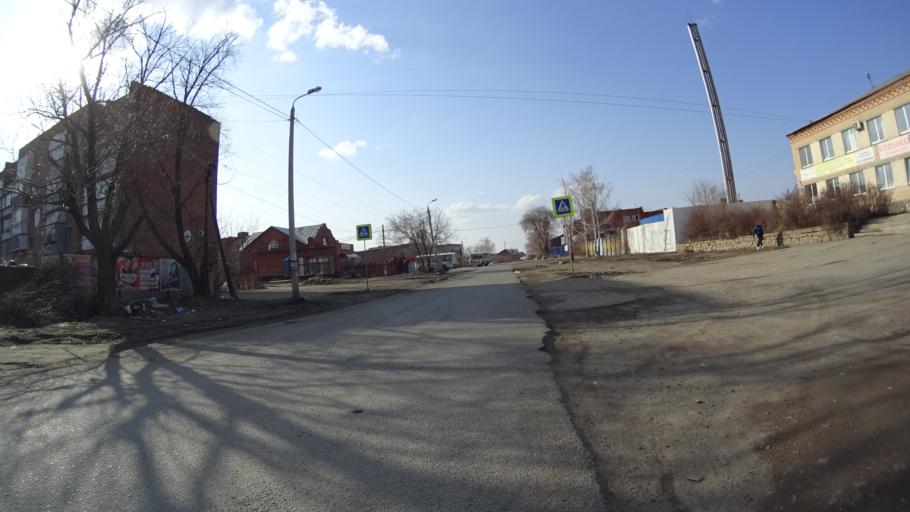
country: RU
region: Chelyabinsk
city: Novosineglazovskiy
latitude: 55.1061
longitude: 61.3379
